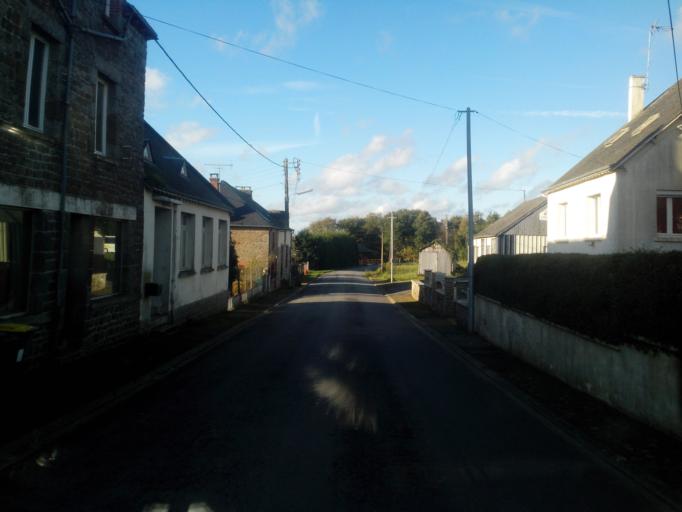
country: FR
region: Brittany
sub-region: Departement du Morbihan
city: Guilliers
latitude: 48.0796
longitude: -2.4119
